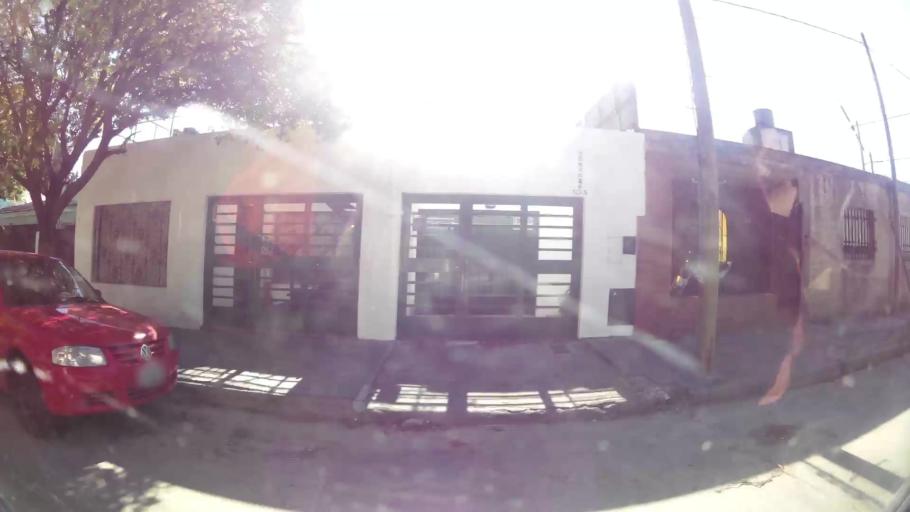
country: AR
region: Cordoba
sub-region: Departamento de Capital
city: Cordoba
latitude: -31.3794
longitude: -64.1894
